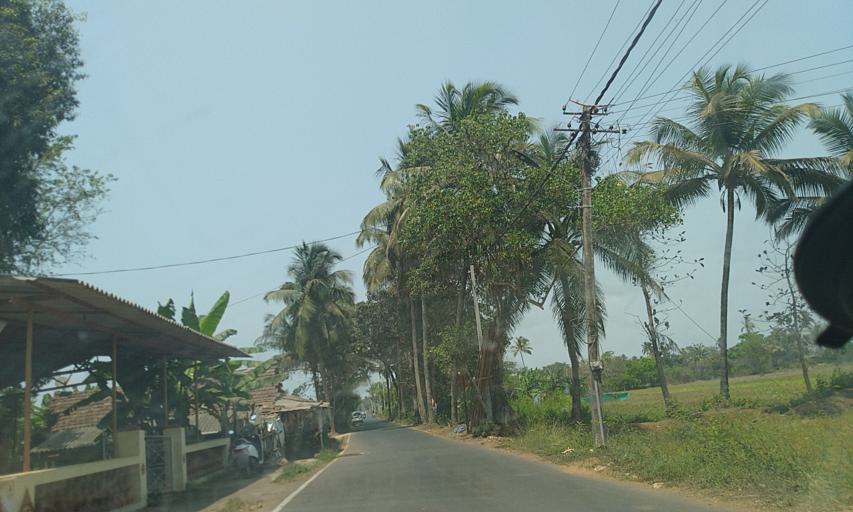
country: IN
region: Goa
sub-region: North Goa
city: Saligao
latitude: 15.5466
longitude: 73.8061
